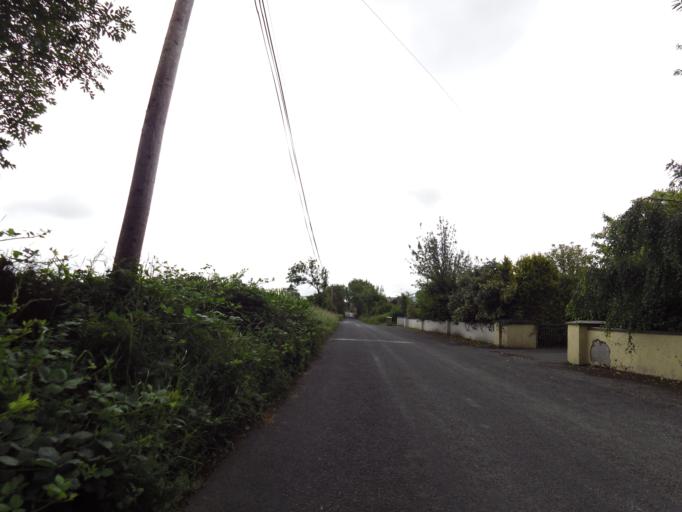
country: IE
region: Connaught
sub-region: County Galway
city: Athenry
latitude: 53.2969
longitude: -8.7113
